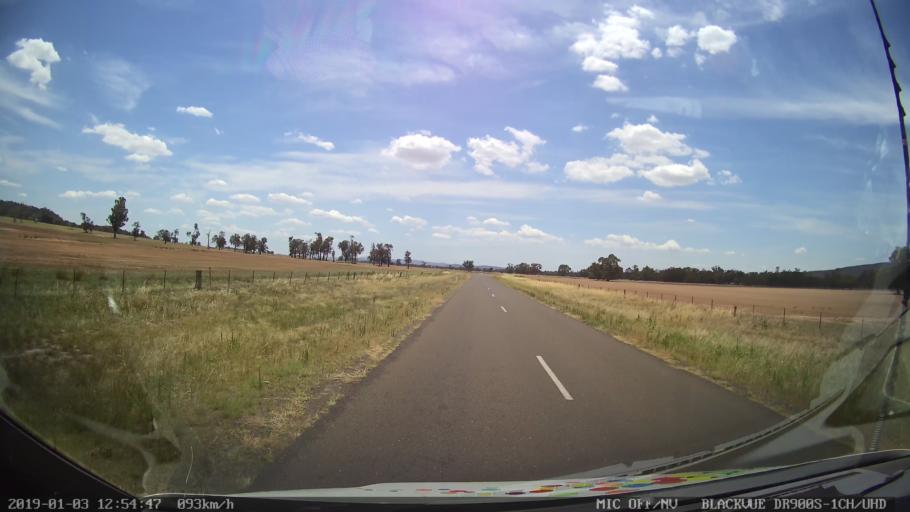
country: AU
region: New South Wales
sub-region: Weddin
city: Grenfell
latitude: -33.6493
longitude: 148.3214
